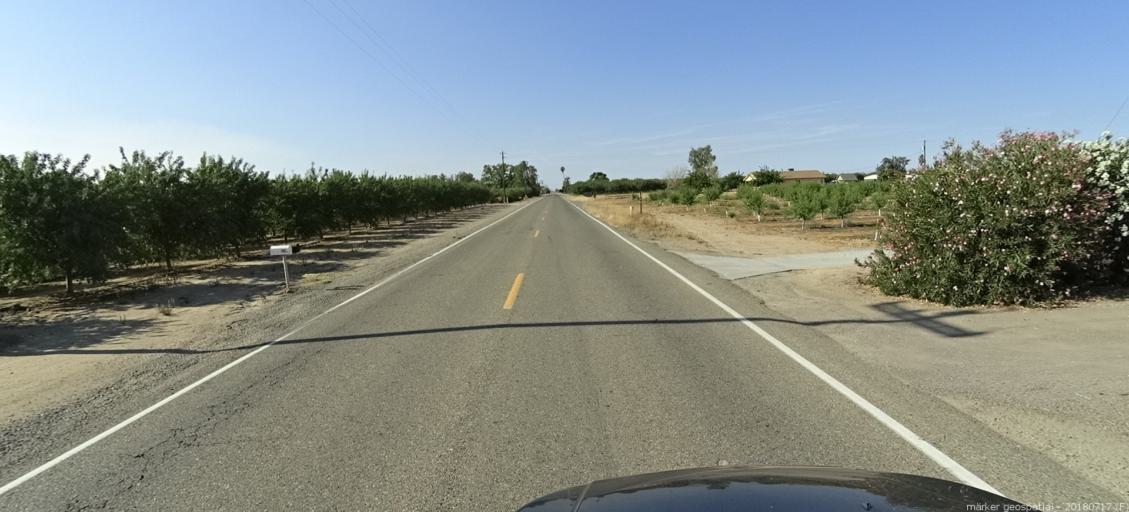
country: US
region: California
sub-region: Madera County
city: Madera Acres
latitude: 37.0357
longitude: -120.1107
